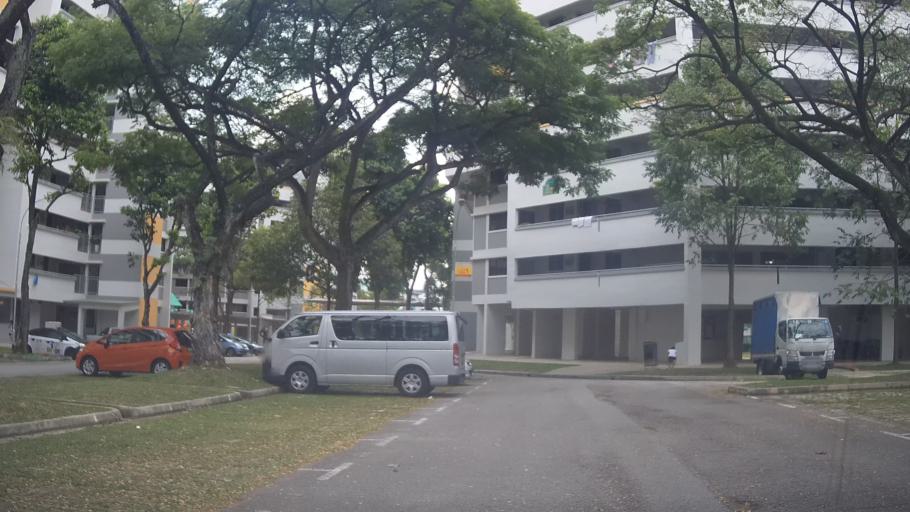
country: SG
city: Singapore
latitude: 1.3590
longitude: 103.8724
